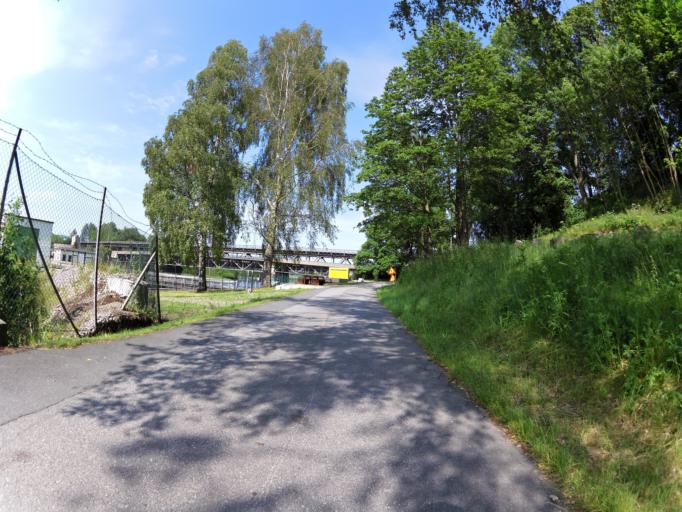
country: NO
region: Ostfold
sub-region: Sarpsborg
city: Sarpsborg
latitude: 59.2754
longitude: 11.1316
